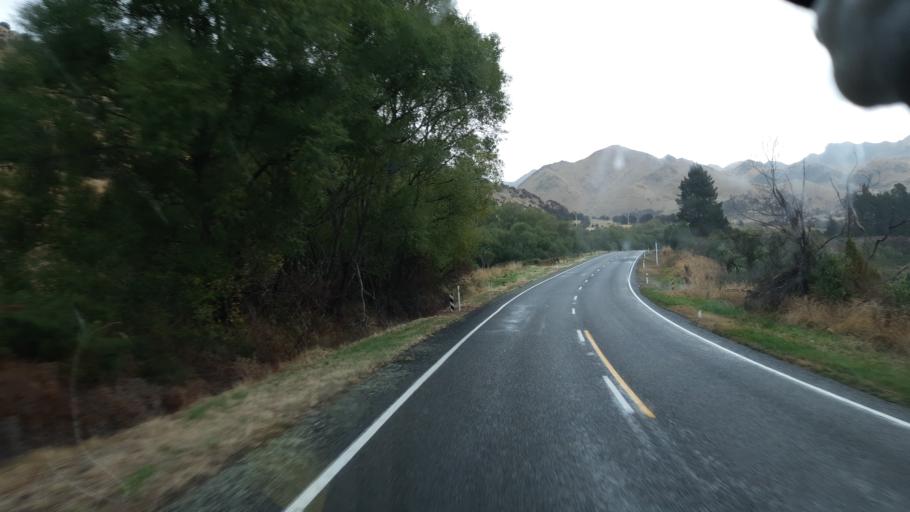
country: NZ
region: Canterbury
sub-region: Hurunui District
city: Amberley
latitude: -42.6699
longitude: 172.7671
